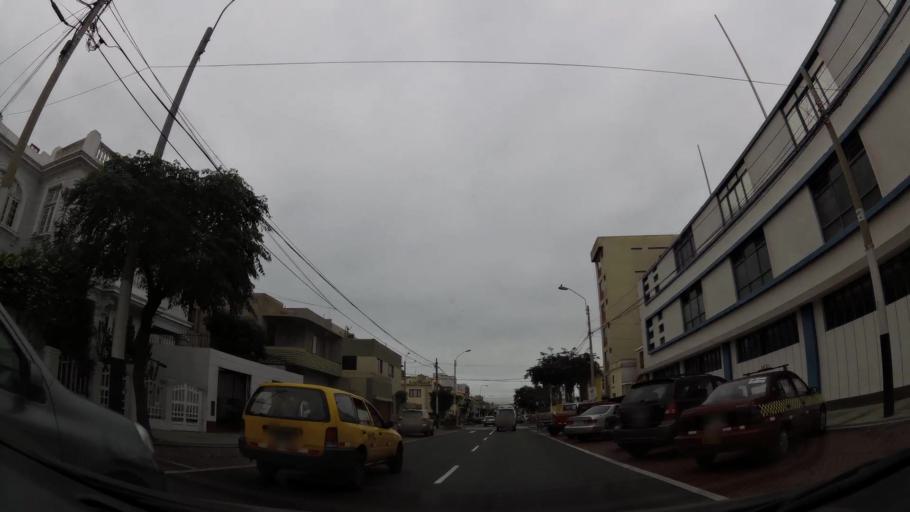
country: PE
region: Callao
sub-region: Callao
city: Callao
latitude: -12.0684
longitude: -77.1597
